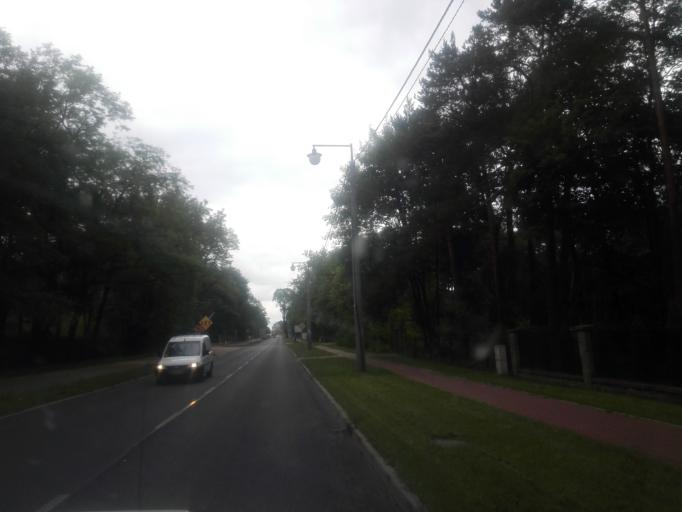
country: PL
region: Silesian Voivodeship
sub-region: Powiat czestochowski
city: Olsztyn
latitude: 50.7443
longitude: 19.2671
